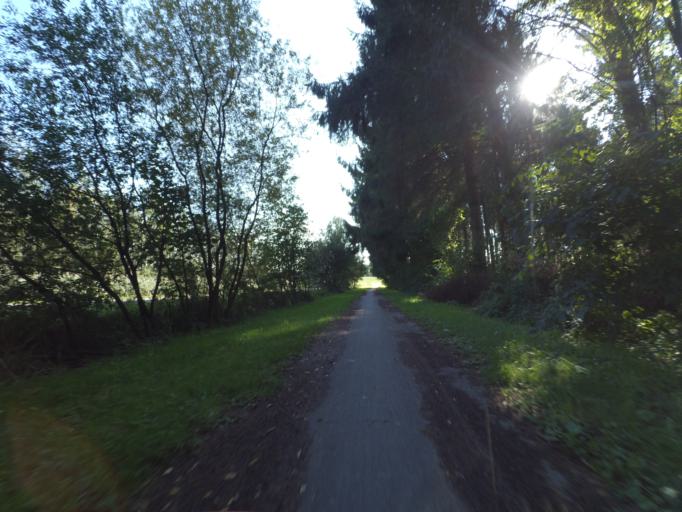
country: NL
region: Flevoland
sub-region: Gemeente Zeewolde
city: Zeewolde
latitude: 52.2756
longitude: 5.5201
